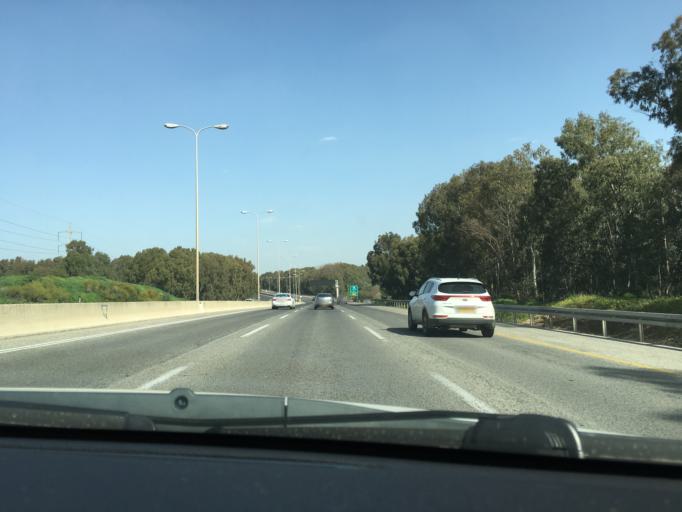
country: IL
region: Central District
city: Hod HaSharon
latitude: 32.1569
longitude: 34.8737
